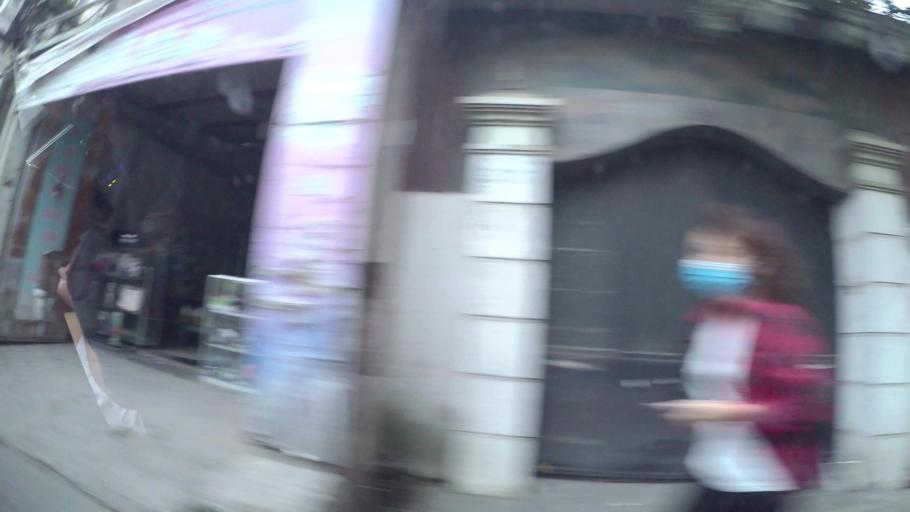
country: VN
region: Ha Noi
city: Hai BaTrung
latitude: 20.9981
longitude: 105.8797
